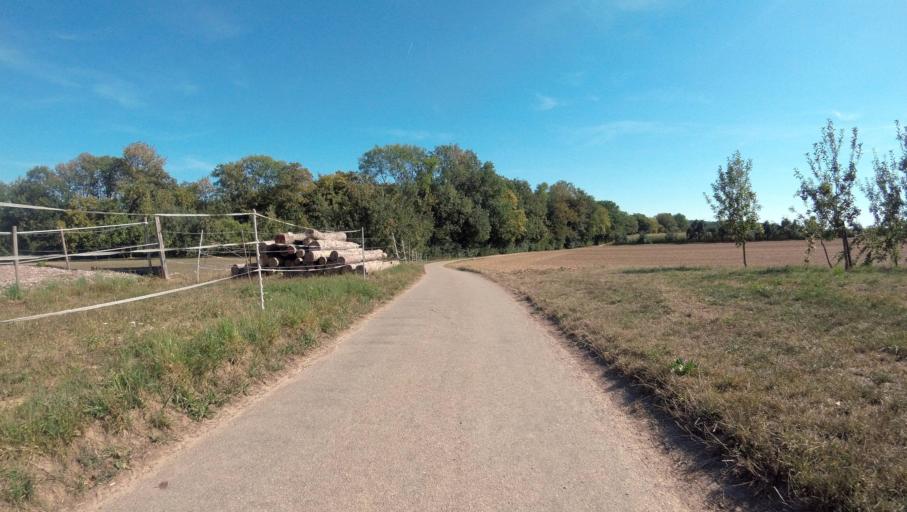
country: DE
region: Baden-Wuerttemberg
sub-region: Regierungsbezirk Stuttgart
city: Mittelschontal
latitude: 48.9424
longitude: 9.3957
